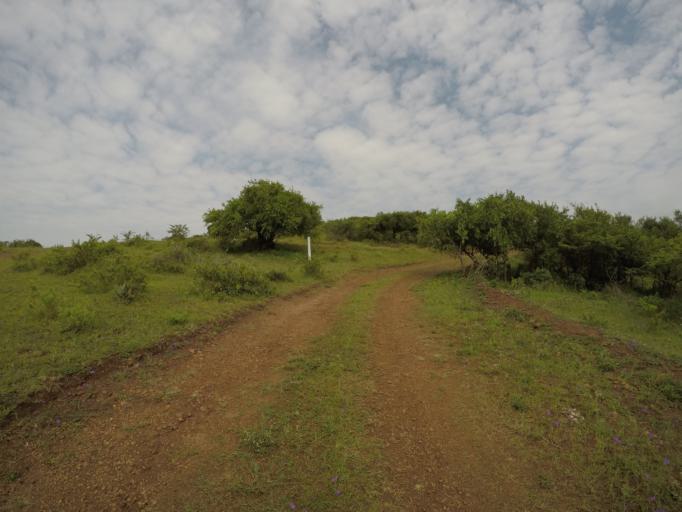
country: ZA
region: KwaZulu-Natal
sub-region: uThungulu District Municipality
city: Empangeni
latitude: -28.6233
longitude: 31.9067
